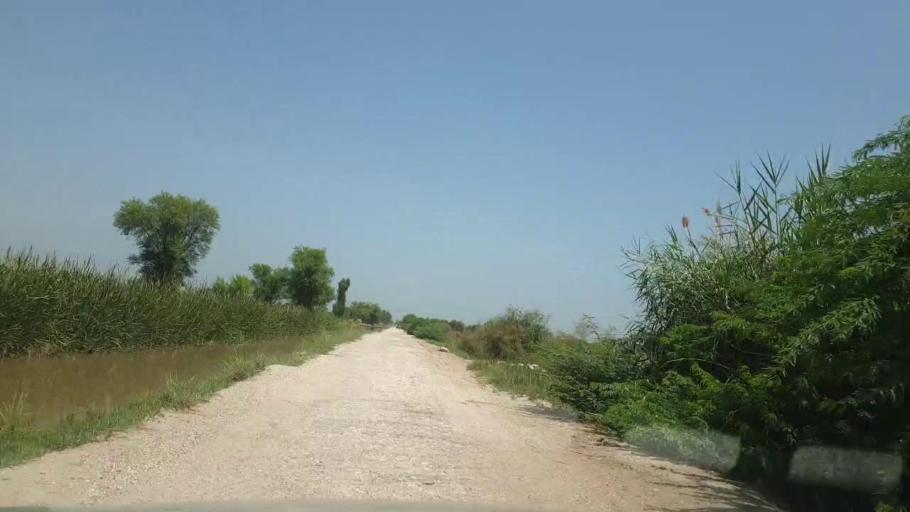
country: PK
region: Sindh
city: Rohri
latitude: 27.6398
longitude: 69.1026
